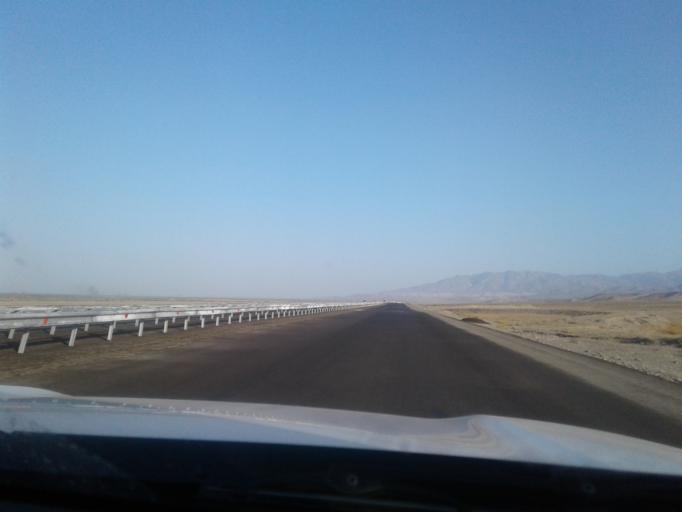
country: TM
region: Balkan
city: Magtymguly
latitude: 38.7080
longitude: 56.8078
